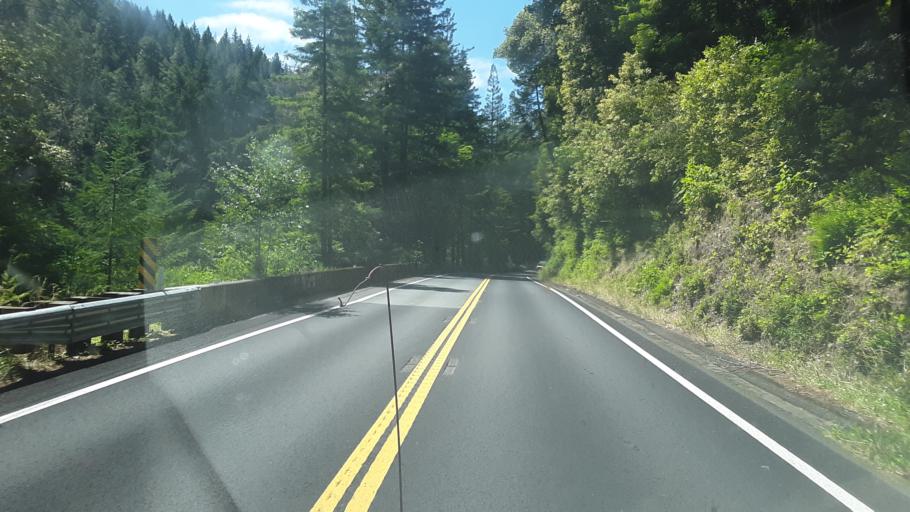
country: US
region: California
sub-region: Del Norte County
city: Bertsch-Oceanview
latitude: 41.8054
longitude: -124.0521
